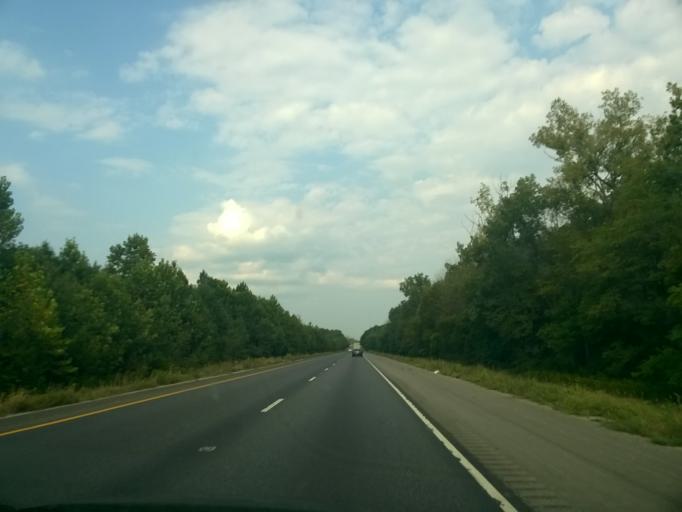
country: US
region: Indiana
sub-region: Clay County
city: Brazil
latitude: 39.4577
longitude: -87.0888
